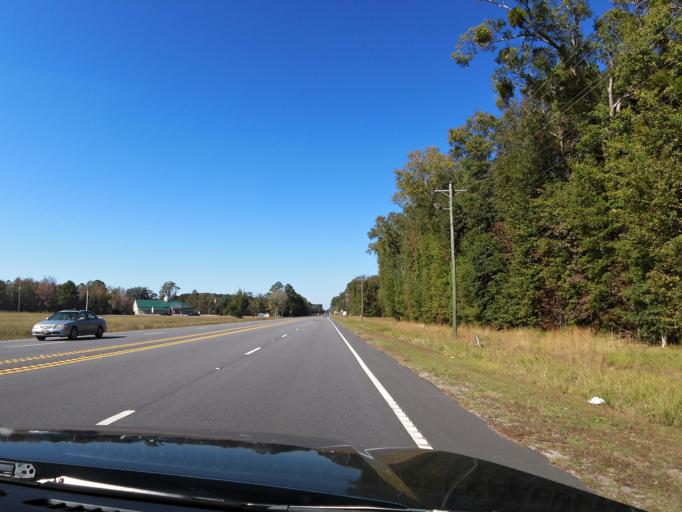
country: US
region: Georgia
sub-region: Liberty County
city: Midway
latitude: 31.7869
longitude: -81.3926
